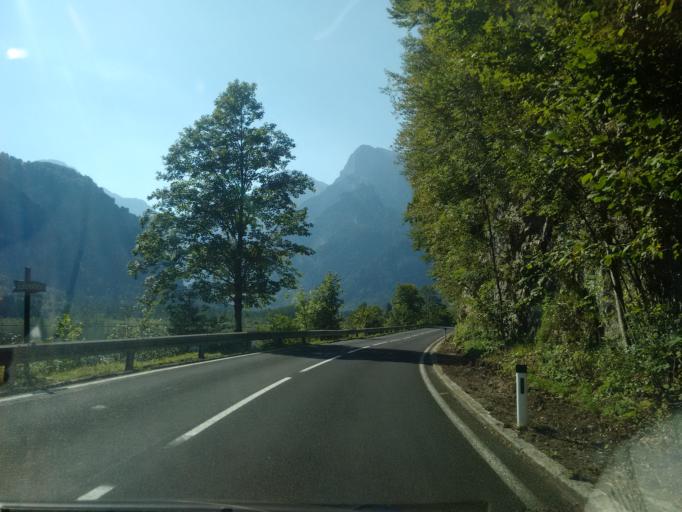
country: AT
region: Upper Austria
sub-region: Politischer Bezirk Gmunden
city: Gruenau im Almtal
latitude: 47.7498
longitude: 13.9532
